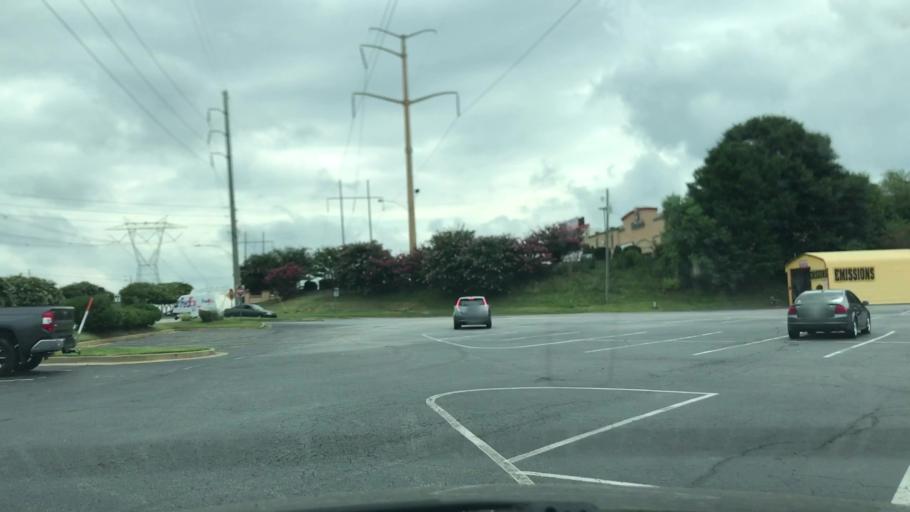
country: US
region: Georgia
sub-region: Gwinnett County
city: Duluth
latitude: 33.9529
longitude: -84.1339
